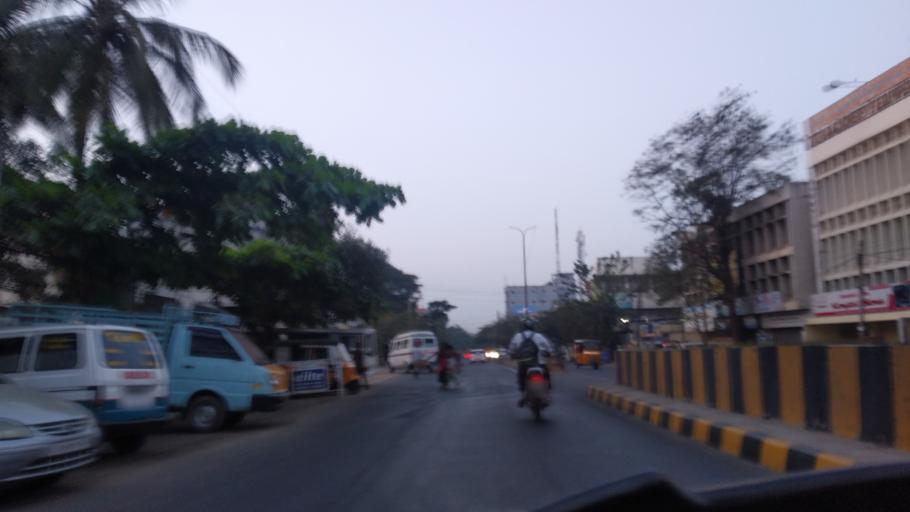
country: IN
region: Tamil Nadu
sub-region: Coimbatore
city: Coimbatore
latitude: 11.0072
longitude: 76.9667
